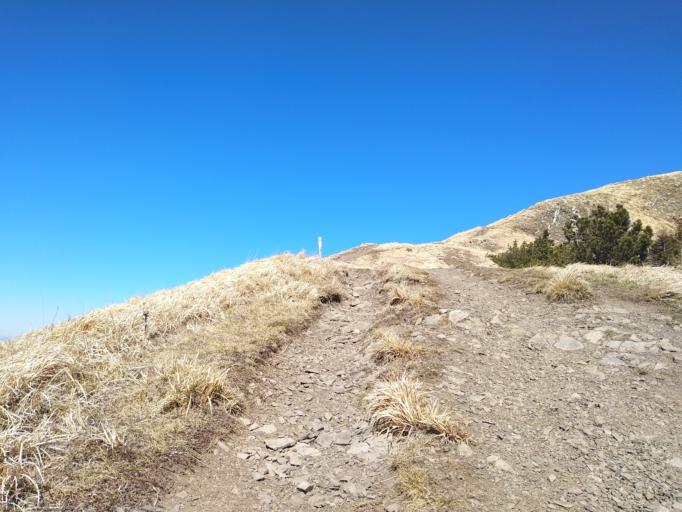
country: IT
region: Emilia-Romagna
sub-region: Provincia di Reggio Emilia
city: Collagna
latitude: 44.3729
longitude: 10.2853
